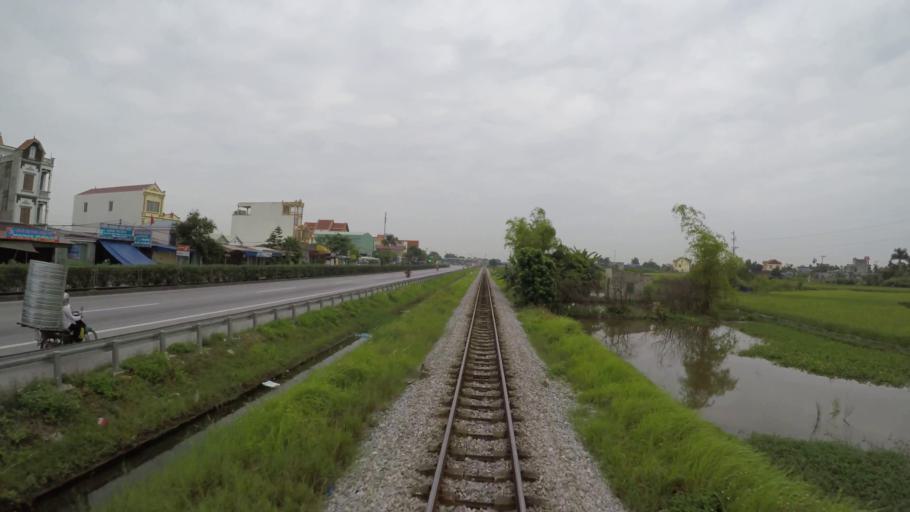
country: VN
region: Hai Duong
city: Phu Thai
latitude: 20.9287
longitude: 106.5551
